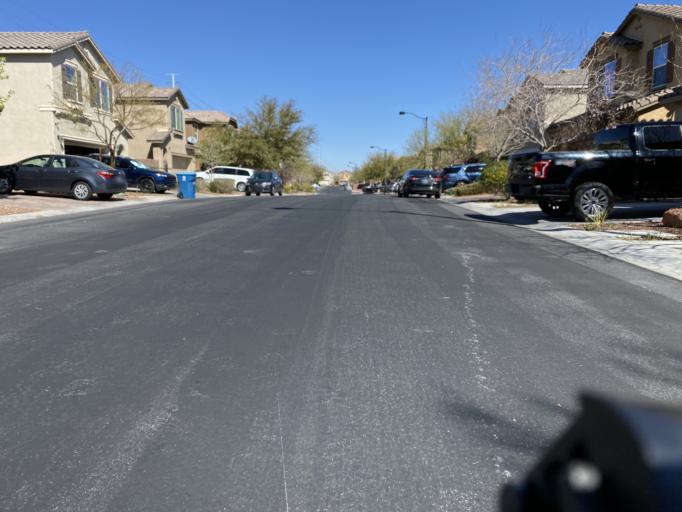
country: US
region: Nevada
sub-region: Clark County
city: Summerlin South
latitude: 36.2999
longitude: -115.3329
